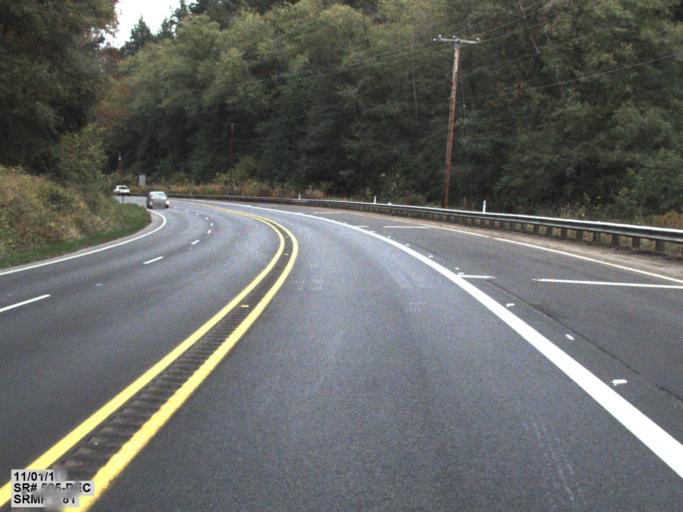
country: US
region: Washington
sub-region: Island County
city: Langley
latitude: 47.9787
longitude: -122.3767
